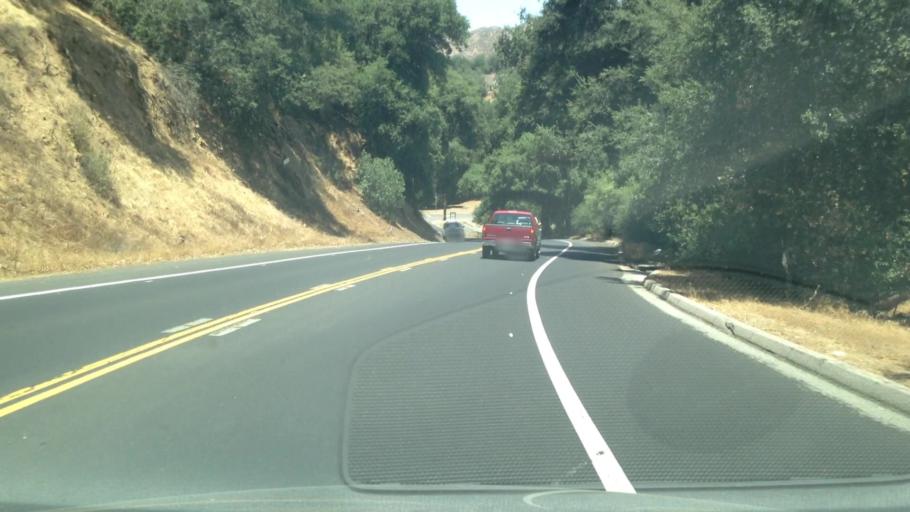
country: US
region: California
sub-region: Riverside County
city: Cherry Valley
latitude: 34.0114
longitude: -116.9940
